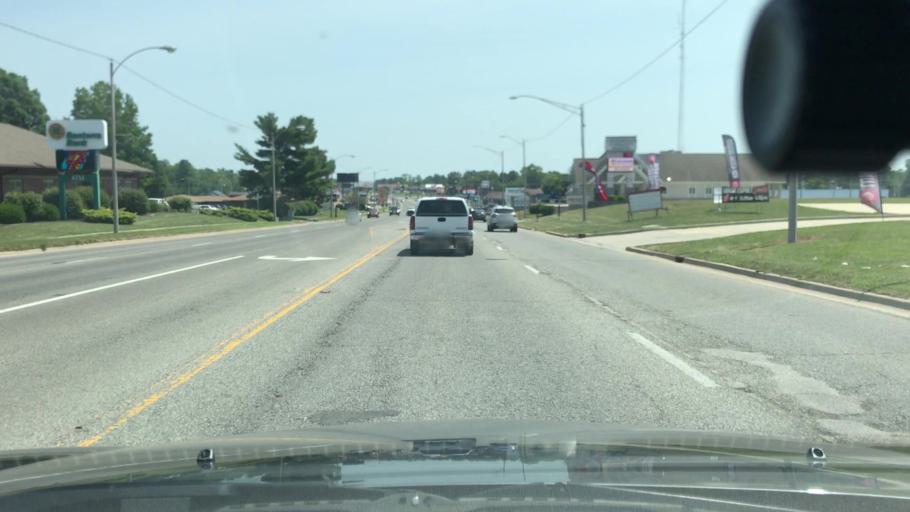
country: US
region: Illinois
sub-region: Jefferson County
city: Mount Vernon
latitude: 38.3143
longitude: -88.9381
